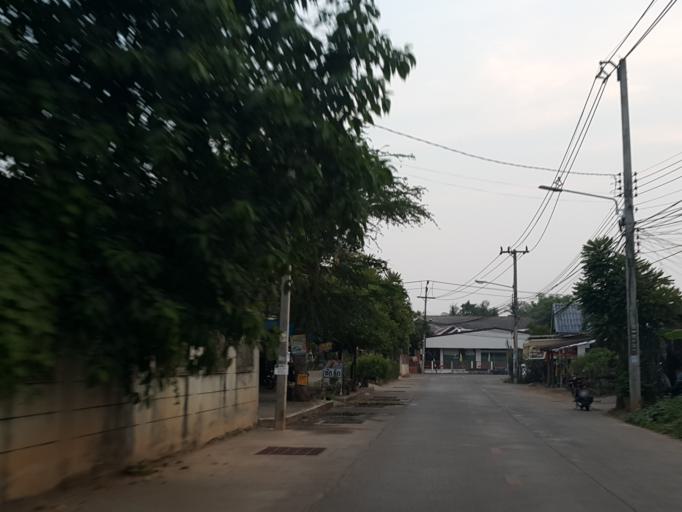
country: TH
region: Sukhothai
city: Sawankhalok
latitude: 17.3128
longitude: 99.8238
